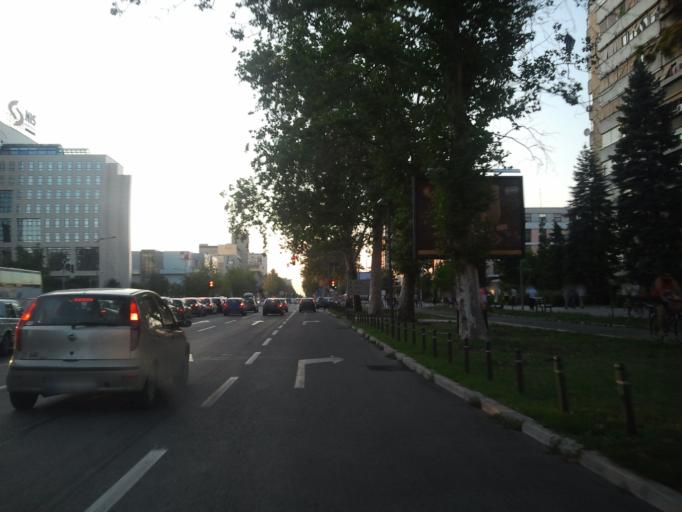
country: RS
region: Autonomna Pokrajina Vojvodina
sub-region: Juznobacki Okrug
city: Novi Sad
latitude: 45.2408
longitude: 19.8433
